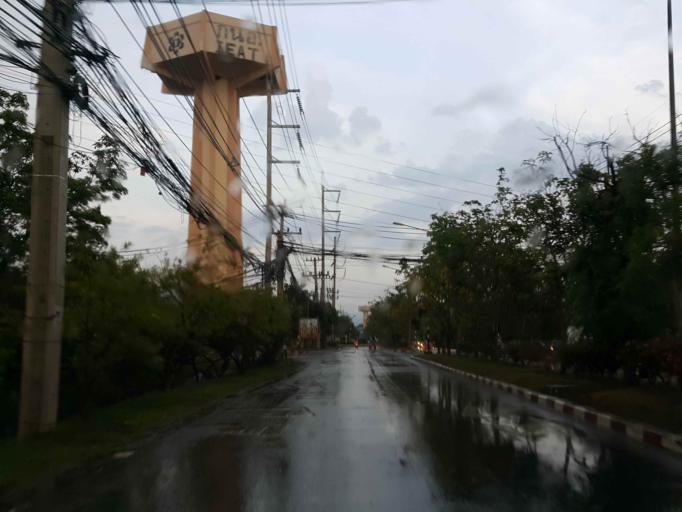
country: TH
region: Lamphun
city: Lamphun
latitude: 18.5891
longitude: 99.0509
